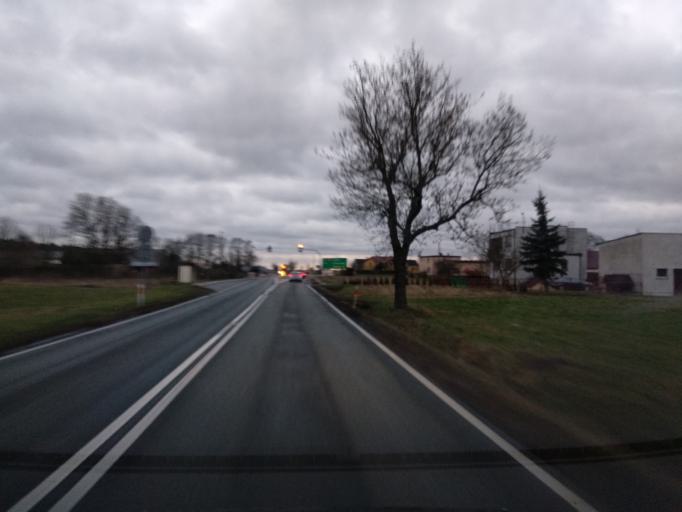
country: PL
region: Greater Poland Voivodeship
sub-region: Powiat koninski
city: Rychwal
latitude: 52.0968
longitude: 18.1670
